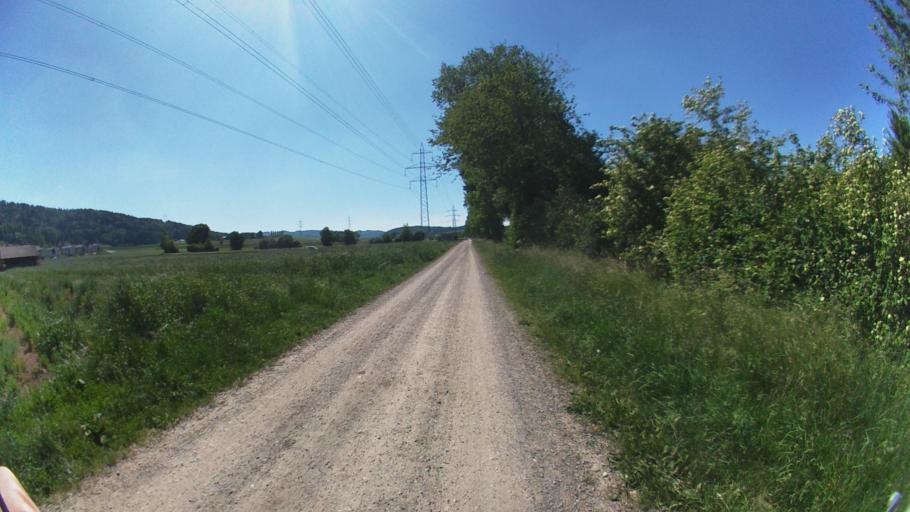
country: CH
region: Zurich
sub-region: Bezirk Dielsdorf
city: Daenikon
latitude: 47.4510
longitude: 8.4050
